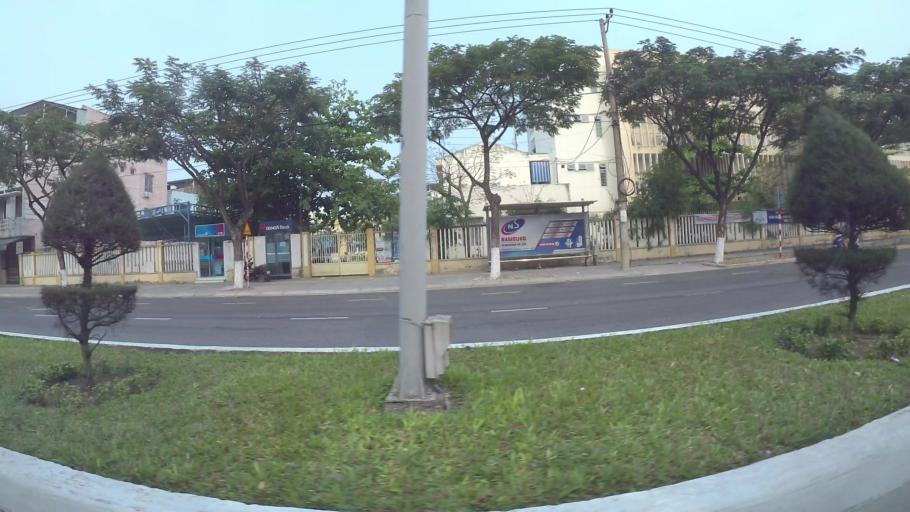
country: VN
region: Da Nang
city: Da Nang
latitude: 16.0444
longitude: 108.2099
